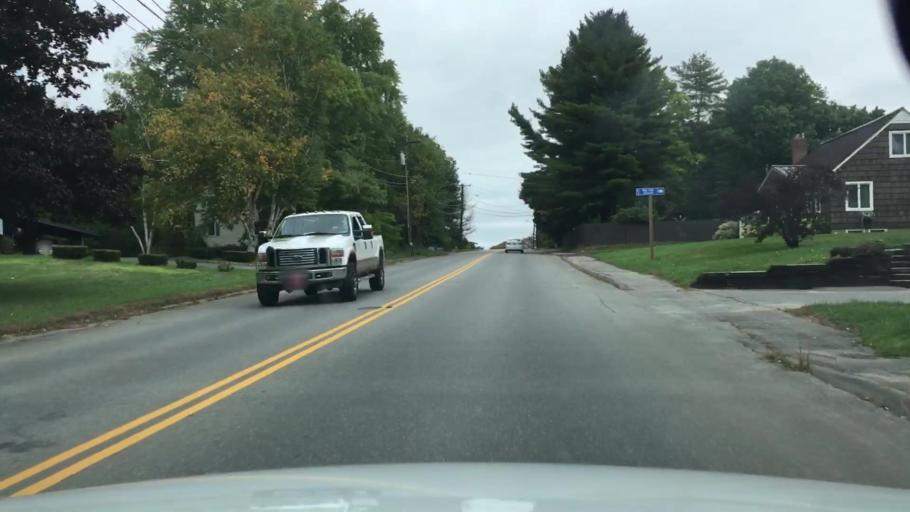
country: US
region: Maine
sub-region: Kennebec County
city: Waterville
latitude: 44.5629
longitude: -69.6402
